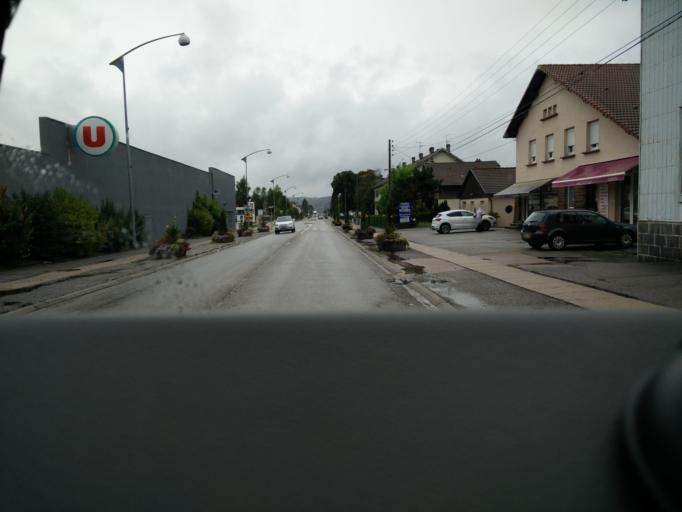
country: FR
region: Lorraine
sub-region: Departement des Vosges
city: Anould
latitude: 48.1919
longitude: 6.9510
